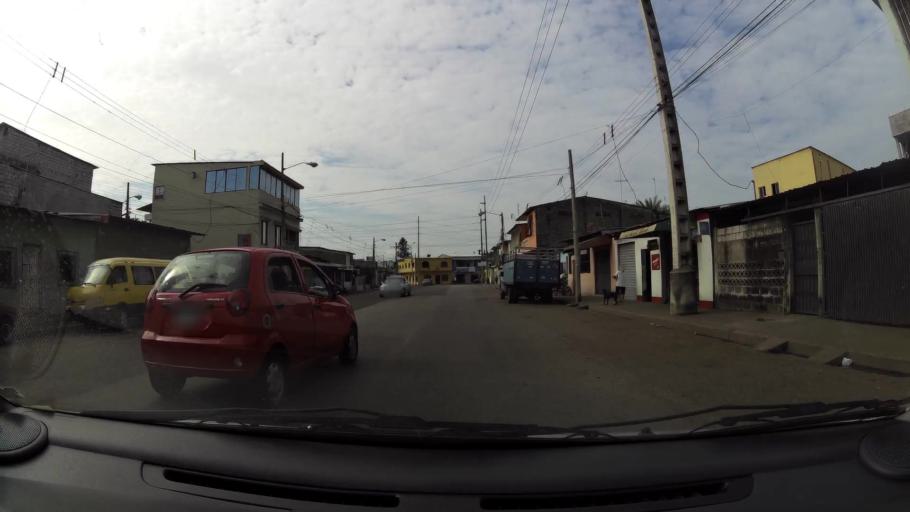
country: EC
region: Guayas
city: Guayaquil
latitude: -2.2506
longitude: -79.8814
